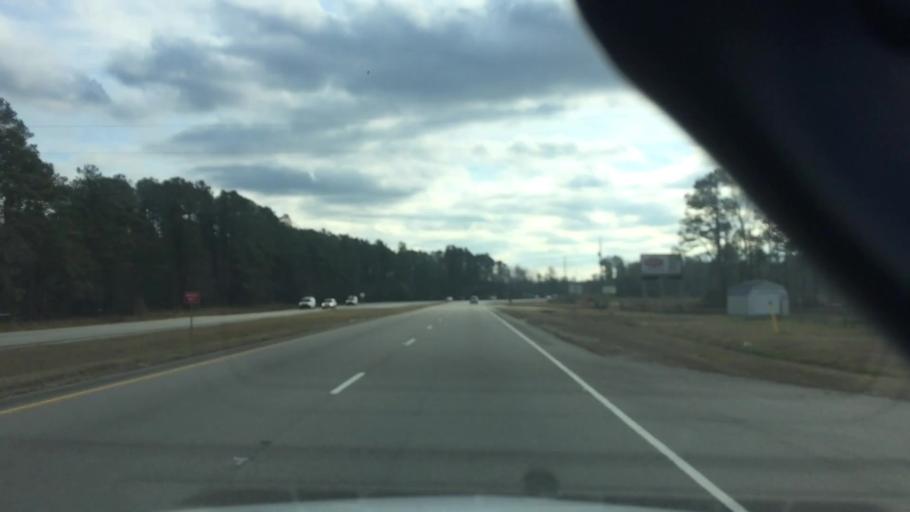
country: US
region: North Carolina
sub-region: Brunswick County
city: Bolivia
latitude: 34.1411
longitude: -78.0940
